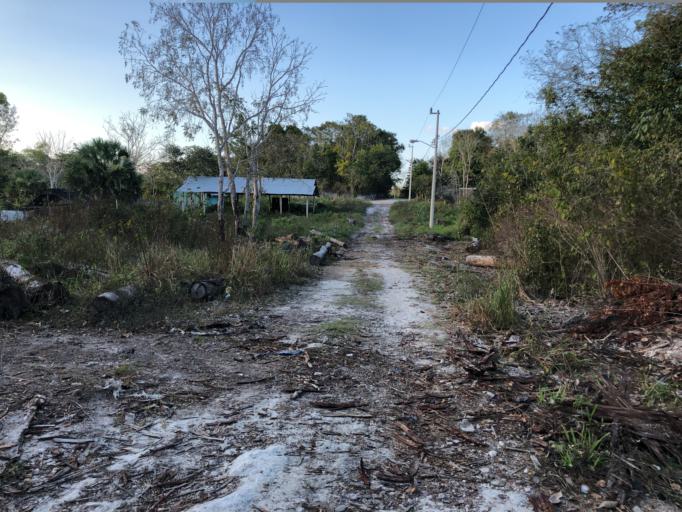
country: MX
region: Quintana Roo
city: Nicolas Bravo
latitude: 18.4487
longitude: -89.3058
